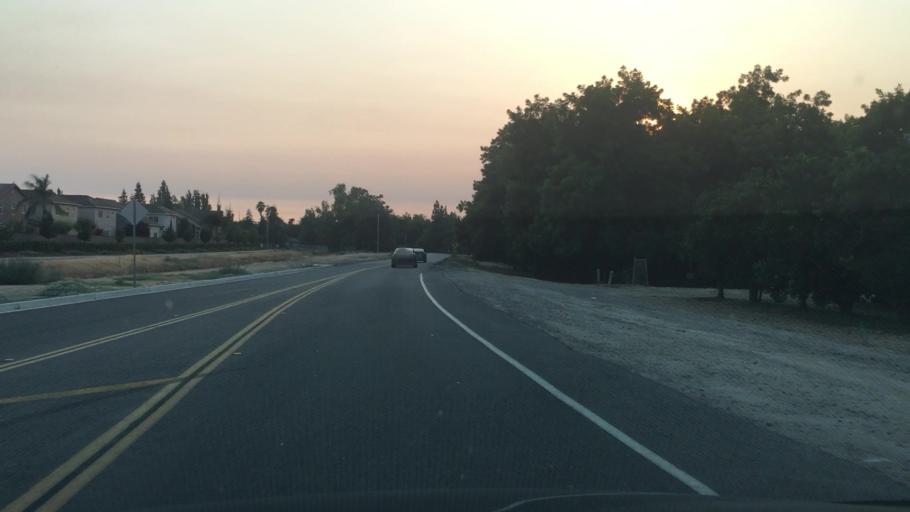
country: US
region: California
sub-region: Fresno County
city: Clovis
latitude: 36.8667
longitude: -119.6859
